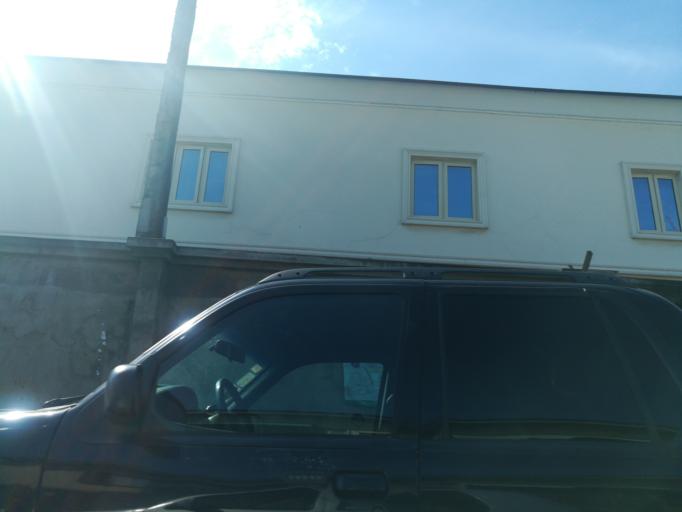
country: NG
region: Lagos
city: Ikeja
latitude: 6.6033
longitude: 3.3431
